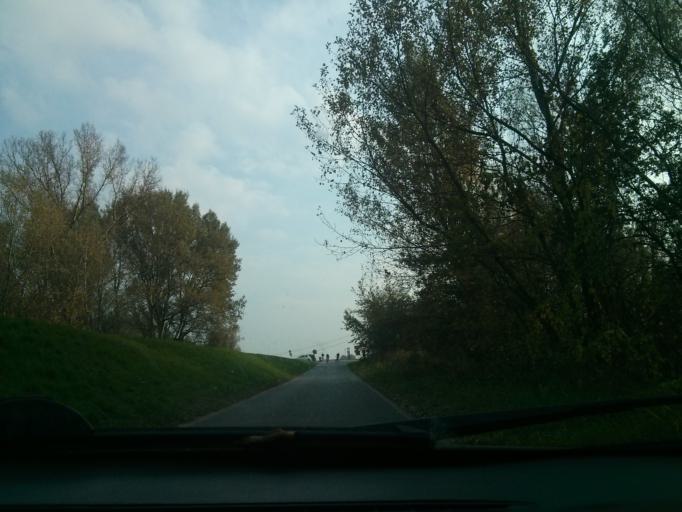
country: PL
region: Masovian Voivodeship
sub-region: Powiat piaseczynski
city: Konstancin-Jeziorna
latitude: 52.1225
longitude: 21.1736
